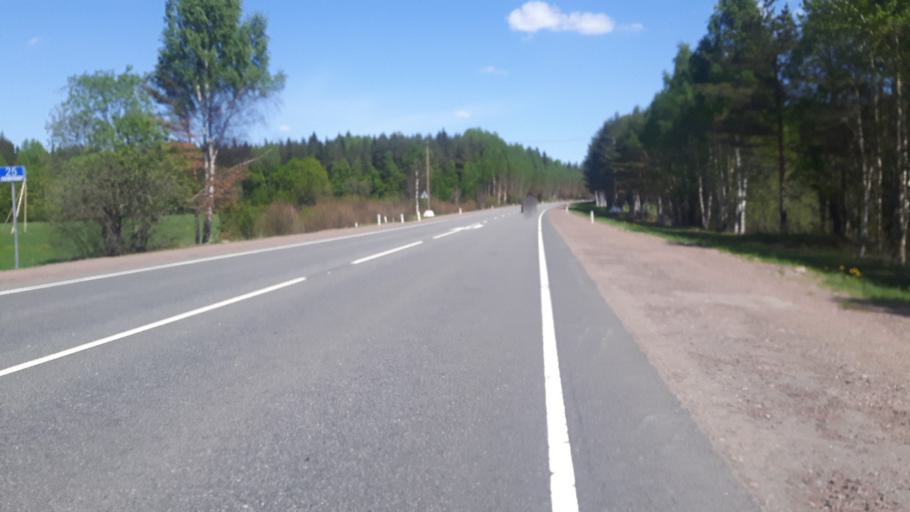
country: RU
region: Leningrad
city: Vysotsk
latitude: 60.6339
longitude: 28.2745
